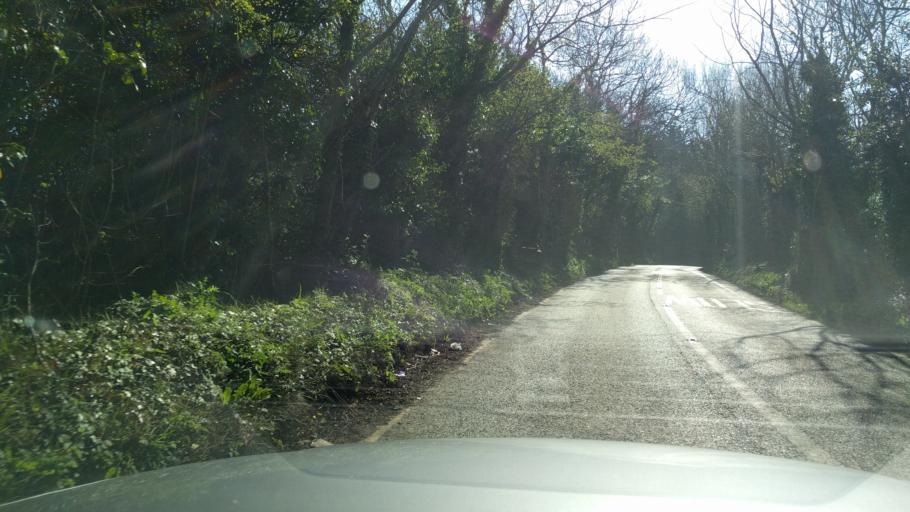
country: IE
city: Knocklyon
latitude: 53.2655
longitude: -6.3259
